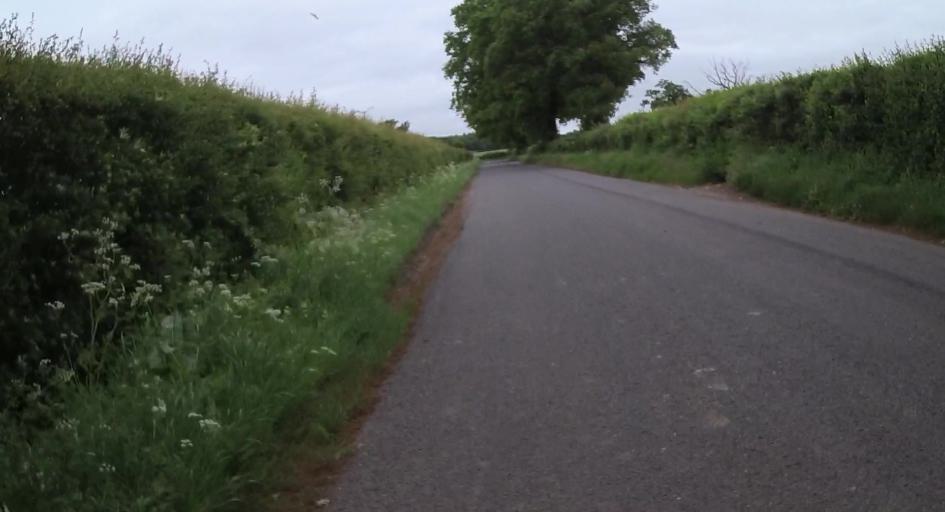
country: GB
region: England
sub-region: West Berkshire
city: Stratfield Mortimer
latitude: 51.3635
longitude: -1.0389
